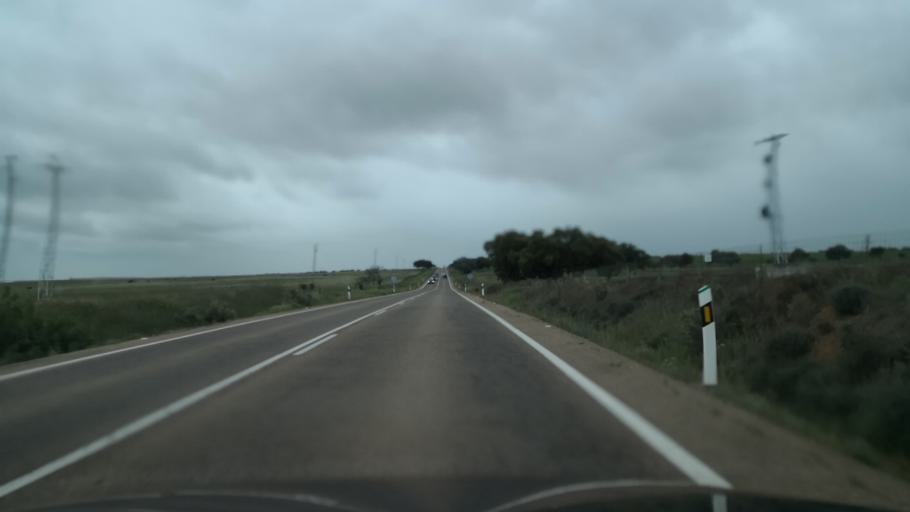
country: ES
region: Extremadura
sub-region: Provincia de Badajoz
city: Badajoz
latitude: 38.9682
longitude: -6.8957
